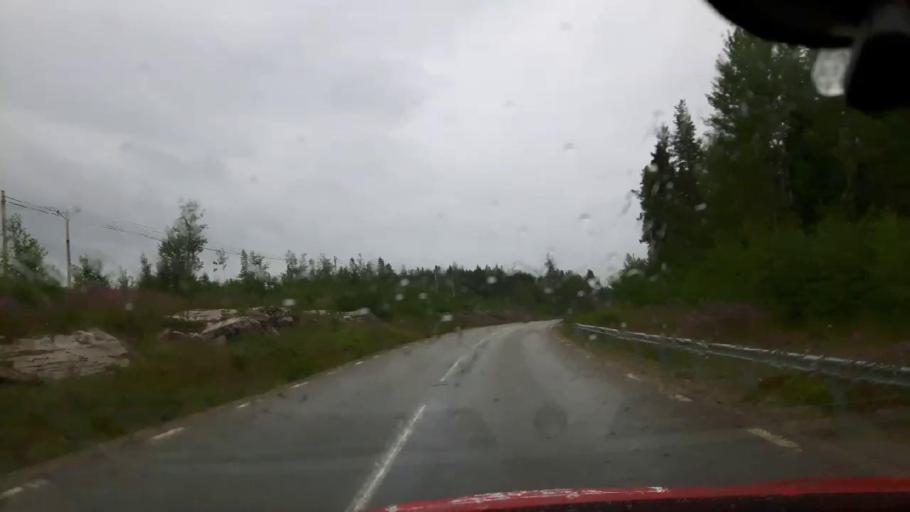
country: SE
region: Jaemtland
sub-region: OEstersunds Kommun
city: Brunflo
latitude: 62.7840
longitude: 15.0098
